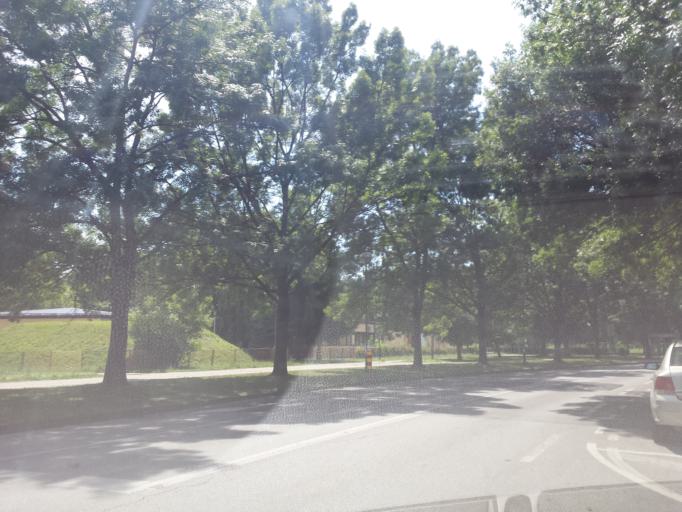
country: HR
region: Grad Zagreb
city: Novi Zagreb
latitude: 45.7692
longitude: 15.9962
